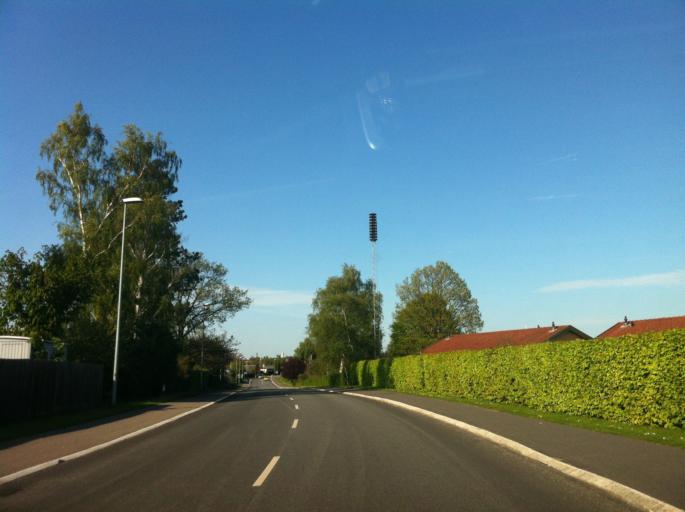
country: DK
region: Zealand
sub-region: Naestved Kommune
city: Naestved
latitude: 55.1960
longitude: 11.7503
